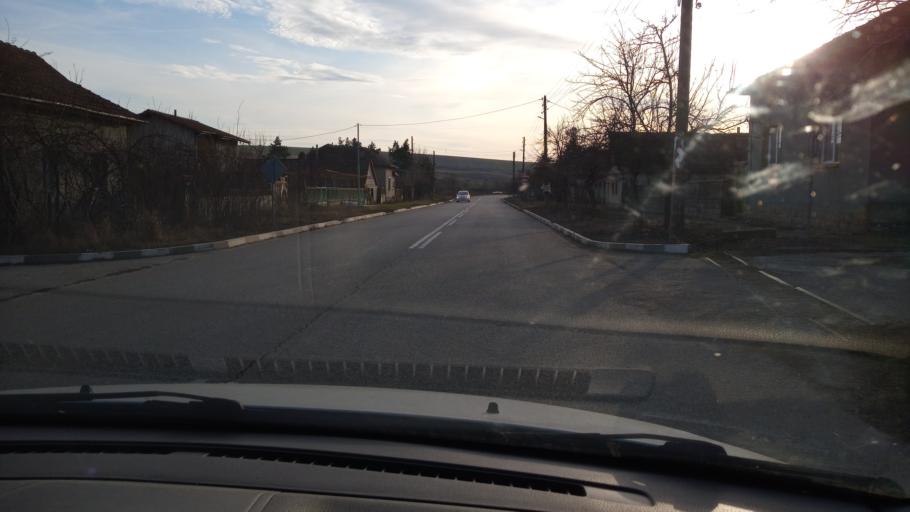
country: BG
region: Pleven
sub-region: Obshtina Pleven
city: Slavyanovo
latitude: 43.5497
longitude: 24.8629
